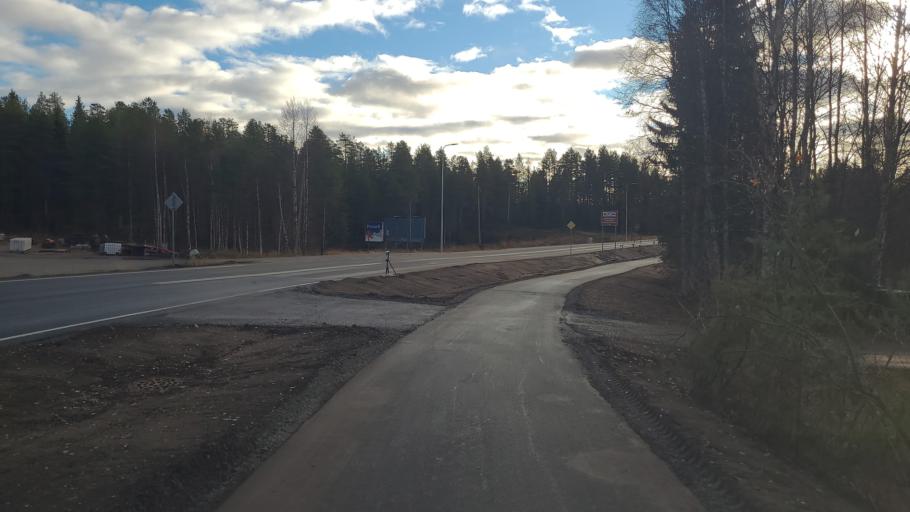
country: FI
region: Lapland
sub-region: Itae-Lappi
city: Posio
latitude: 66.1086
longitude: 28.1773
